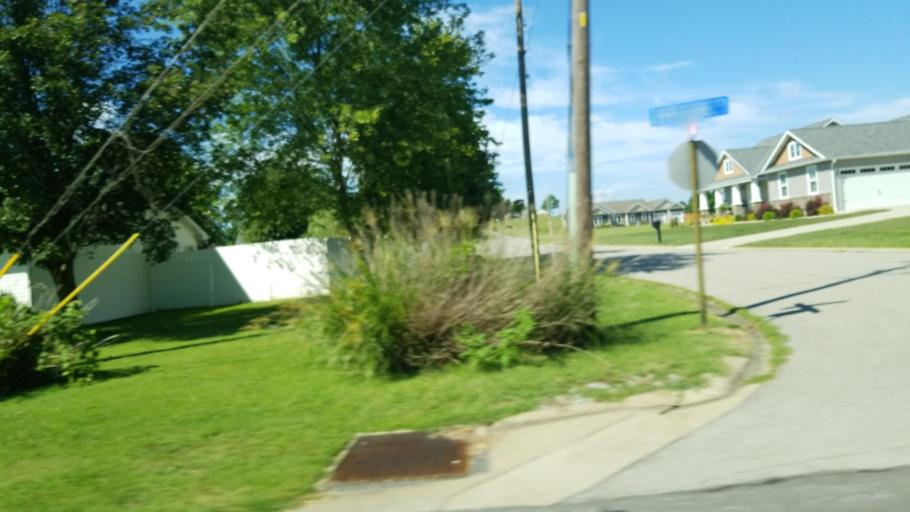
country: US
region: Illinois
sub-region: Williamson County
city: Marion
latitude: 37.7427
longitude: -88.8970
